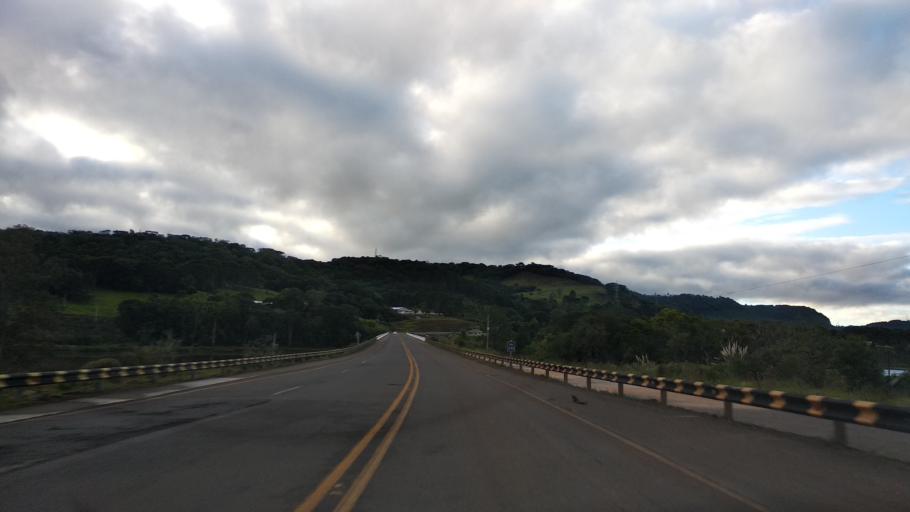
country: BR
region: Santa Catarina
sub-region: Curitibanos
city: Curitibanos
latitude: -27.5377
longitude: -50.8646
